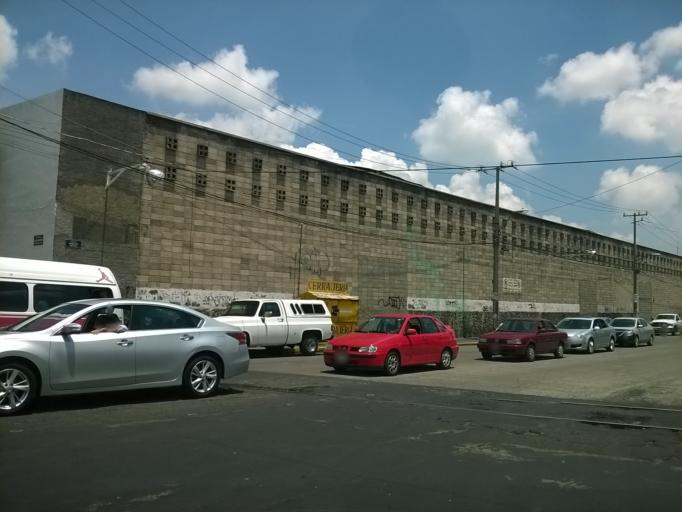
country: MX
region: Michoacan
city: Morelia
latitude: 19.7071
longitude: -101.1979
